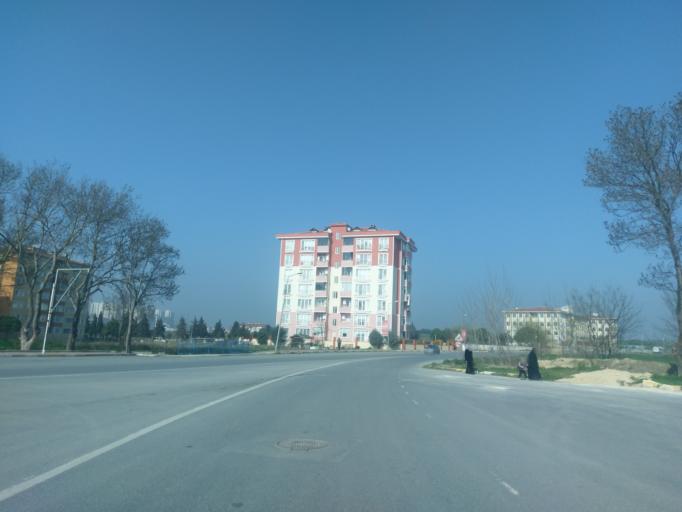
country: TR
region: Istanbul
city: Silivri
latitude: 41.0833
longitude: 28.2631
